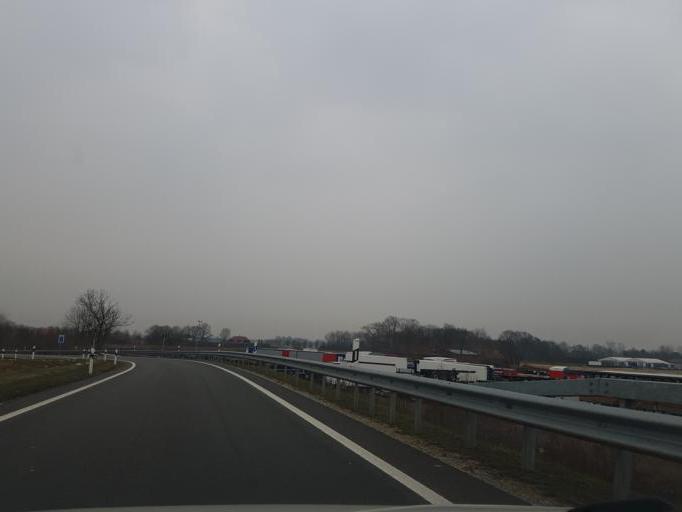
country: DE
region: Lower Saxony
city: Geeste
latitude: 52.6656
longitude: 7.1799
